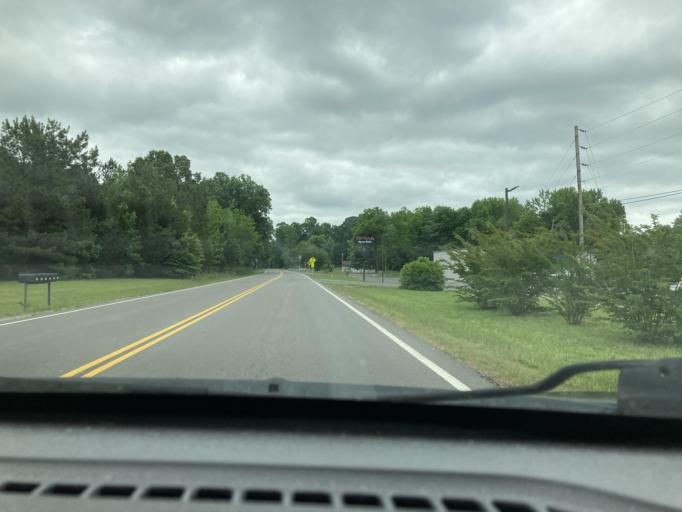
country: US
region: Tennessee
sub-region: Dickson County
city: Burns
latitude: 36.0333
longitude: -87.3493
